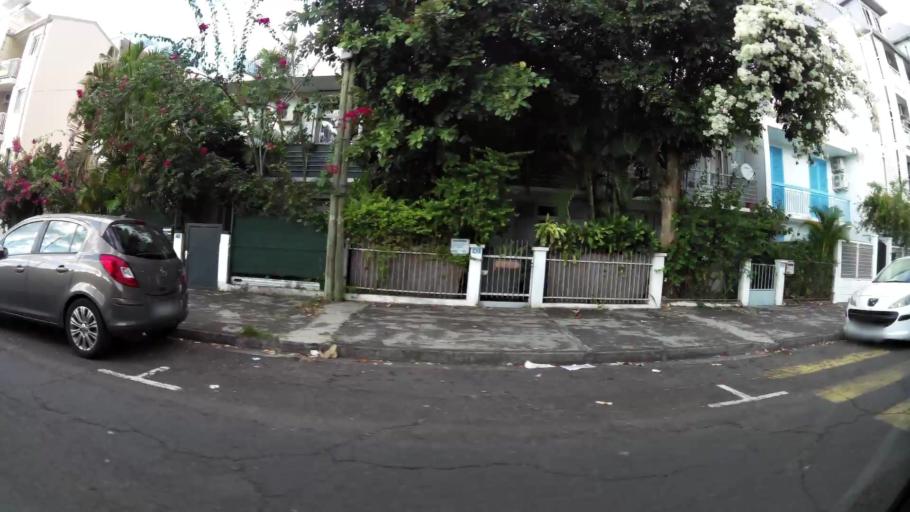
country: RE
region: Reunion
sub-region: Reunion
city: Saint-Denis
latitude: -20.8849
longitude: 55.4566
